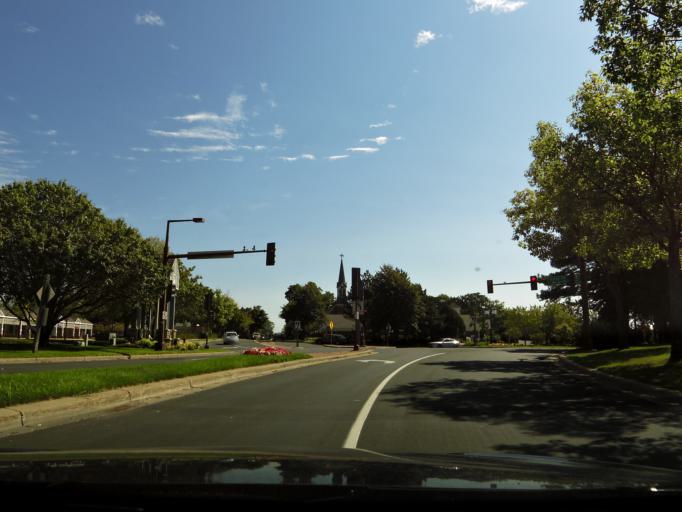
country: US
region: Minnesota
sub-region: Carver County
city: Chanhassen
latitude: 44.8621
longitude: -93.5330
